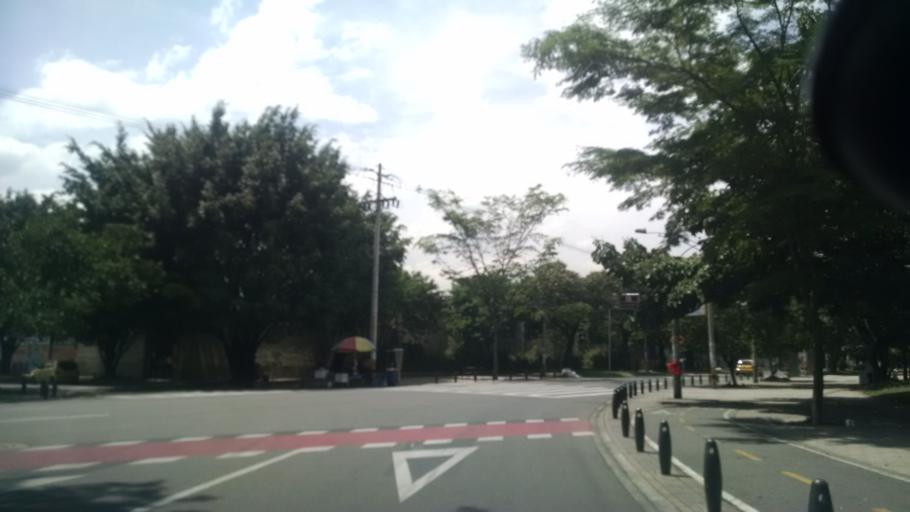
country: CO
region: Antioquia
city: Medellin
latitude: 6.2582
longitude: -75.5864
